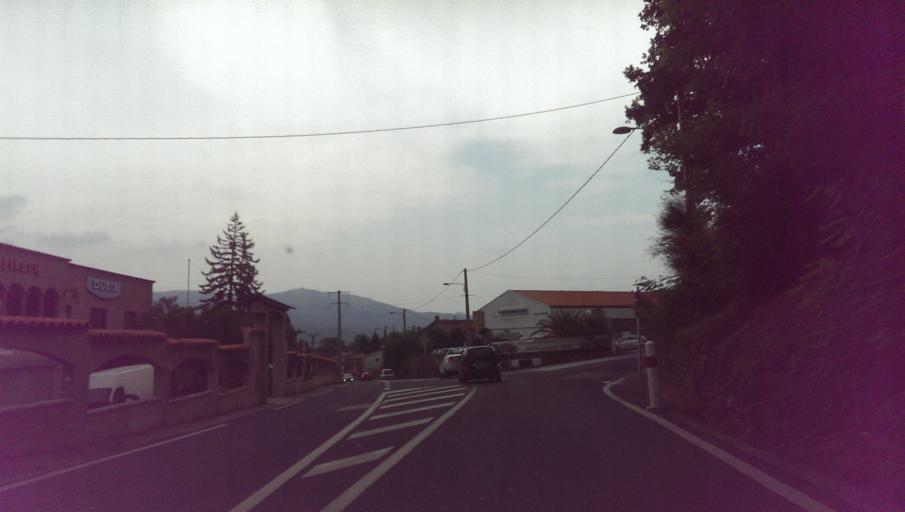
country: FR
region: Languedoc-Roussillon
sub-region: Departement des Pyrenees-Orientales
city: Ria-Sirach
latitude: 42.6106
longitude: 2.4086
